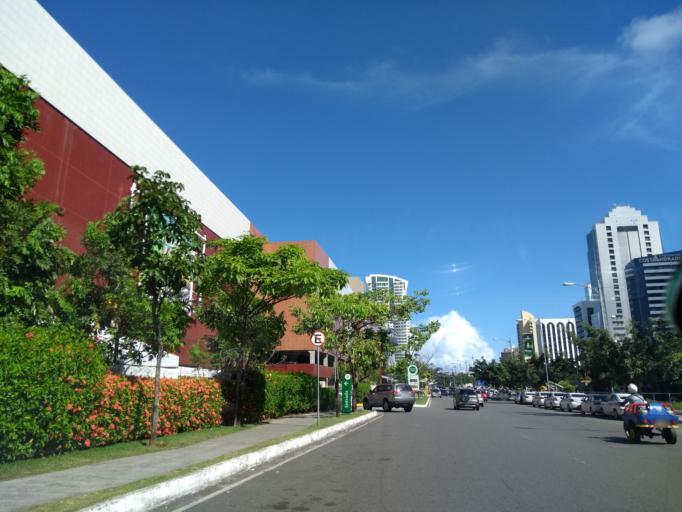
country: BR
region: Bahia
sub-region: Salvador
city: Salvador
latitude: -12.9780
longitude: -38.4569
